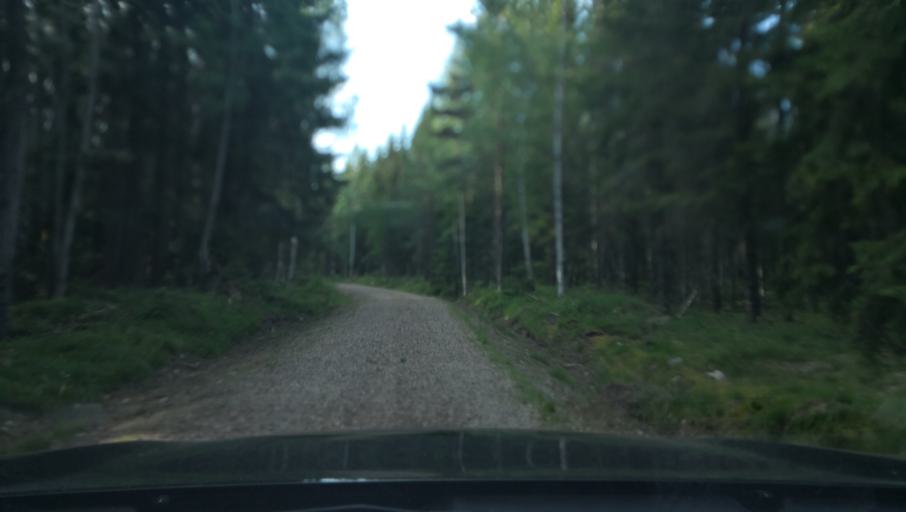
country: SE
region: Dalarna
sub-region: Ludvika Kommun
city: Ludvika
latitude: 60.0743
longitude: 15.2906
